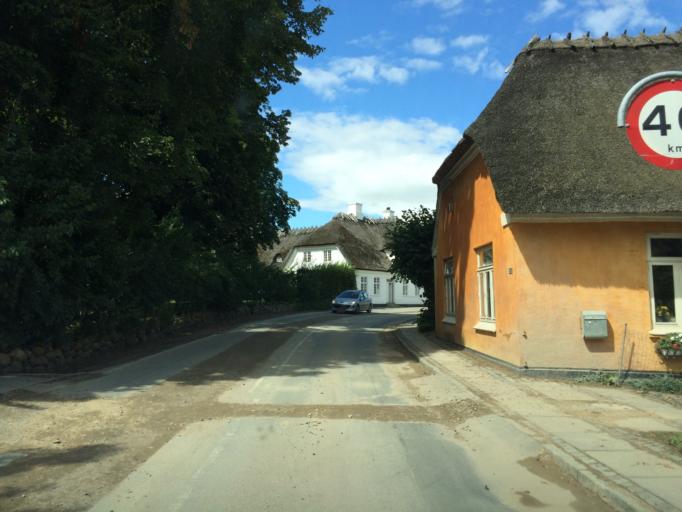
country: DK
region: South Denmark
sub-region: Assens Kommune
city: Harby
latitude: 55.1523
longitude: 10.1488
